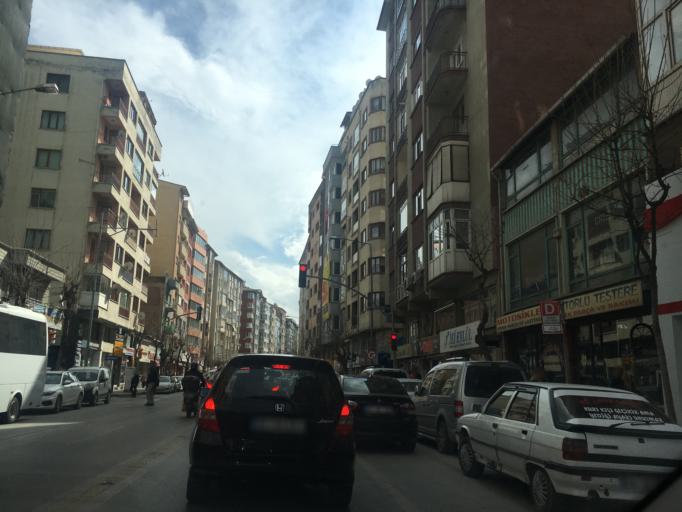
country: TR
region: Eskisehir
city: Eskisehir
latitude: 39.7798
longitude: 30.5153
